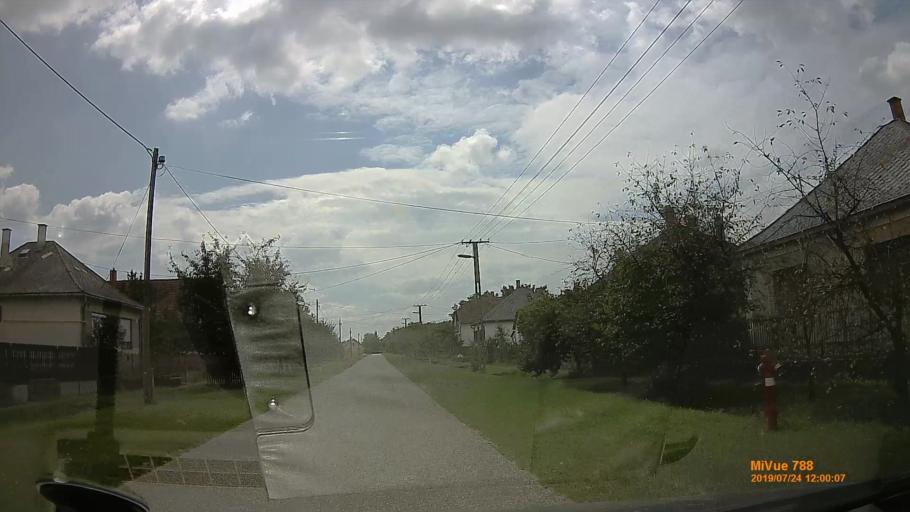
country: HU
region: Szabolcs-Szatmar-Bereg
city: Tarpa
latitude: 48.1991
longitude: 22.4516
